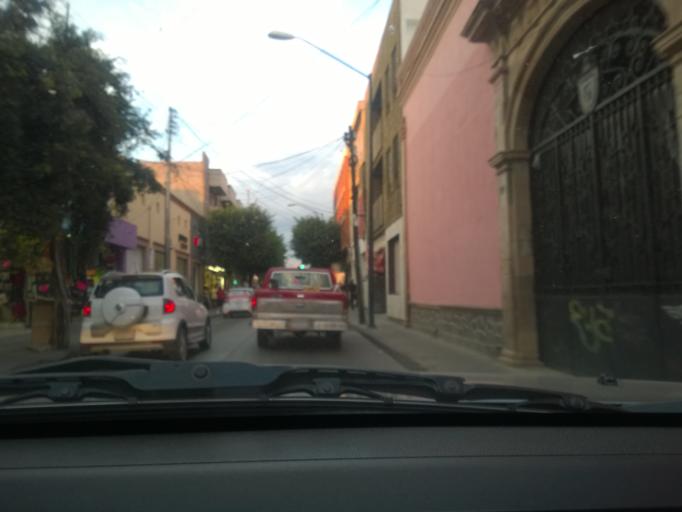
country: MX
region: Guanajuato
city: Leon
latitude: 21.1254
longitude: -101.6841
